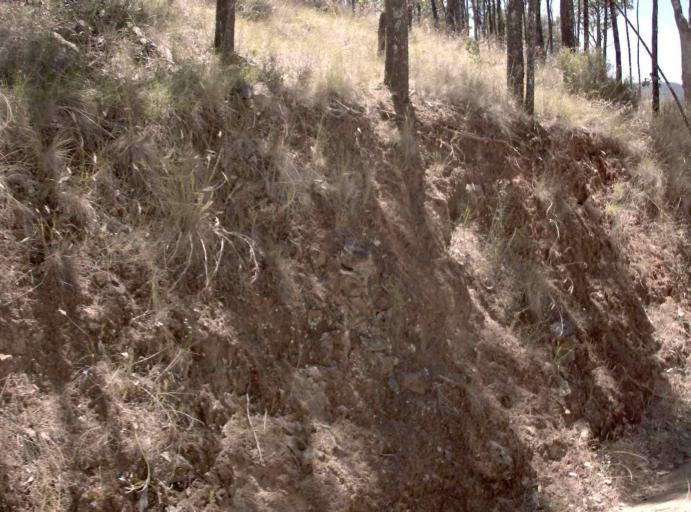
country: AU
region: New South Wales
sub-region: Snowy River
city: Jindabyne
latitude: -36.9061
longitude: 148.4162
